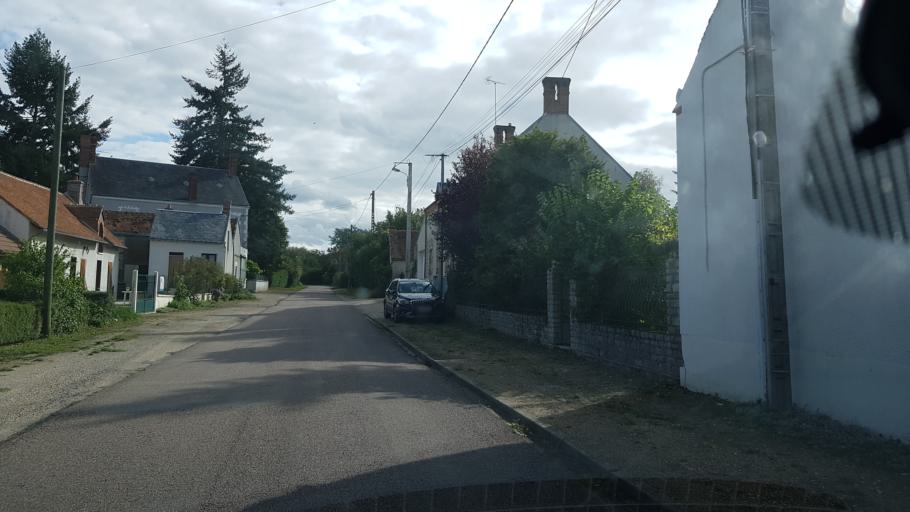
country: FR
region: Centre
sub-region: Departement du Loiret
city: Chilleurs-aux-Bois
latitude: 48.0630
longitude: 2.2140
